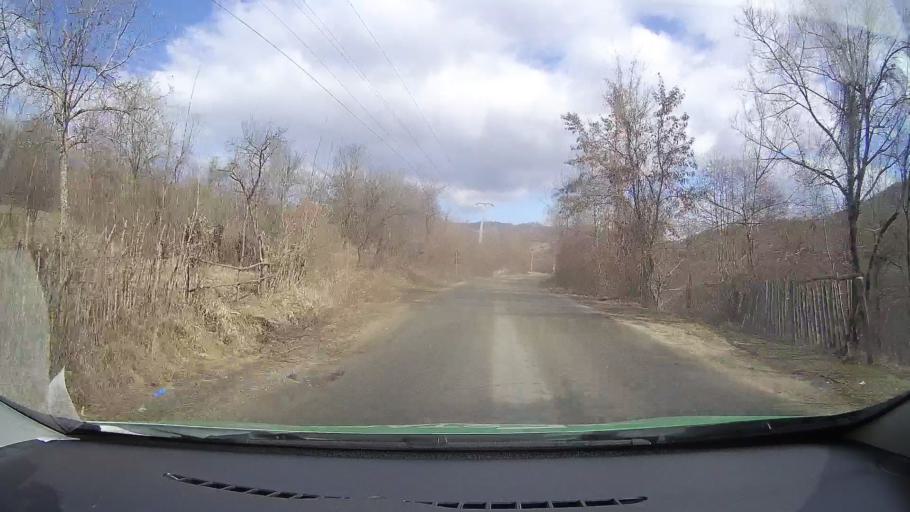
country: RO
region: Dambovita
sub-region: Comuna Motaeni
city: Motaeni
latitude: 45.1097
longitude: 25.4412
